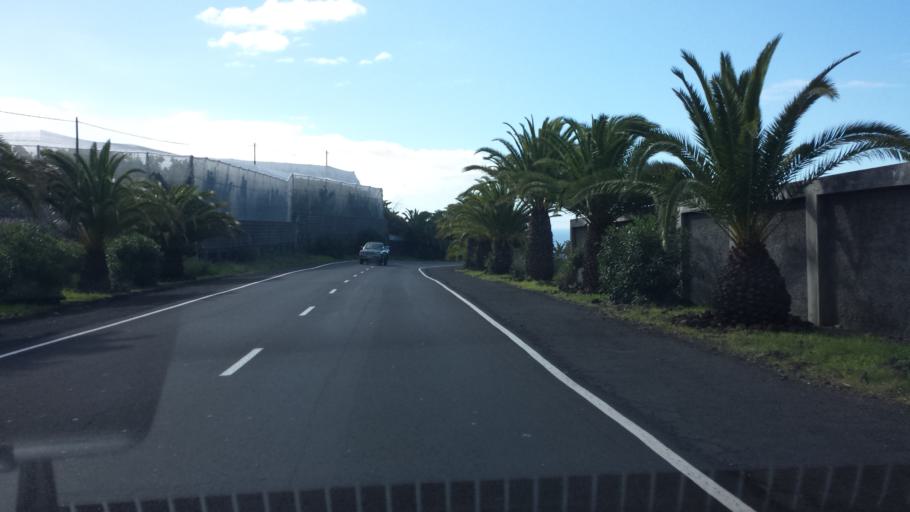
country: ES
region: Canary Islands
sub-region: Provincia de Santa Cruz de Tenerife
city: Tazacorte
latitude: 28.6064
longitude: -17.9069
